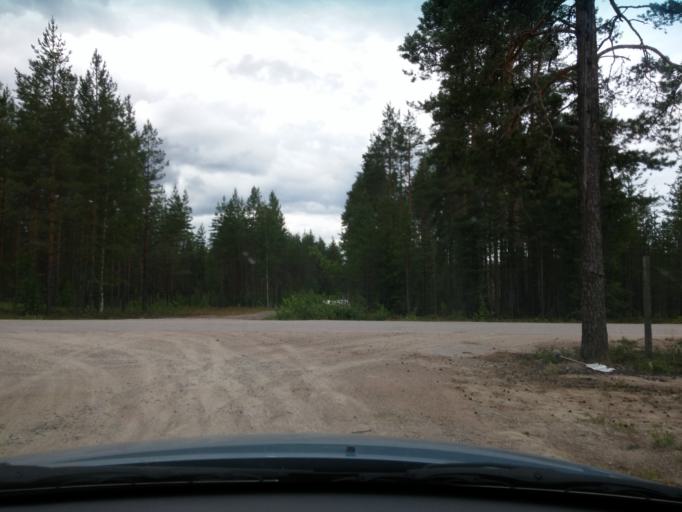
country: FI
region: Central Finland
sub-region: AEaenekoski
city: AEaenekoski
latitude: 62.7596
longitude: 25.6780
